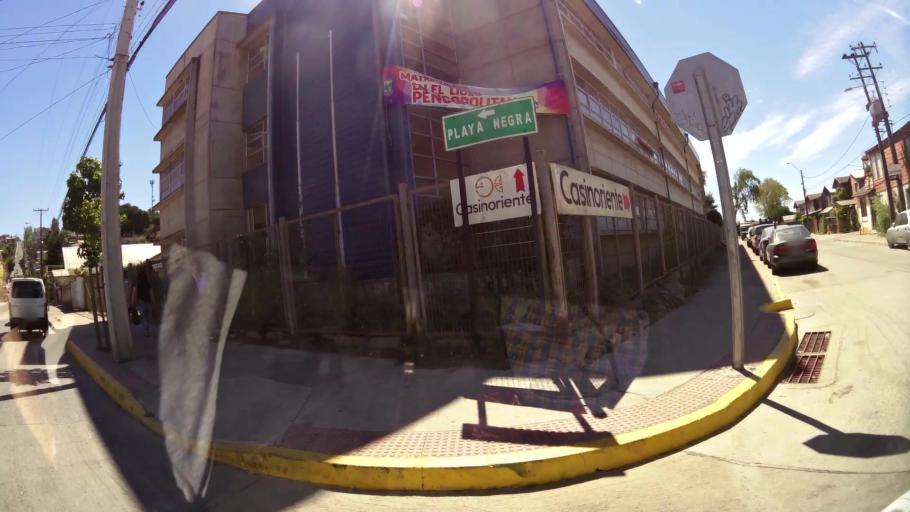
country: CL
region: Biobio
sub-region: Provincia de Concepcion
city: Penco
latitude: -36.7388
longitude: -72.9992
